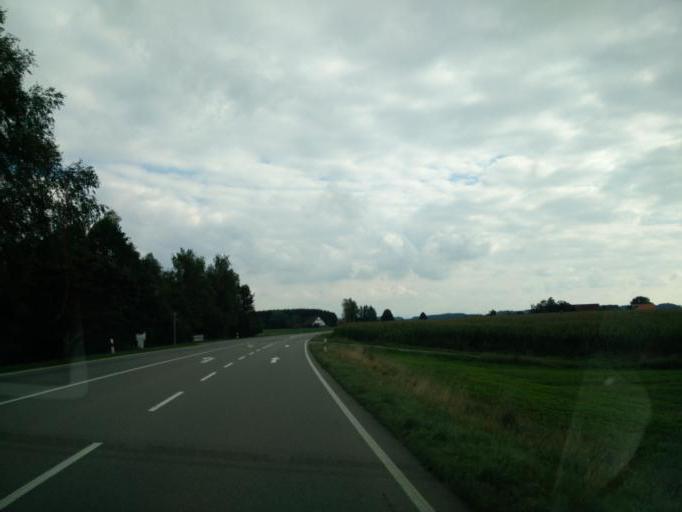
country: DE
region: Baden-Wuerttemberg
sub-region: Tuebingen Region
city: Bad Wurzach
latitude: 47.8860
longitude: 9.9078
